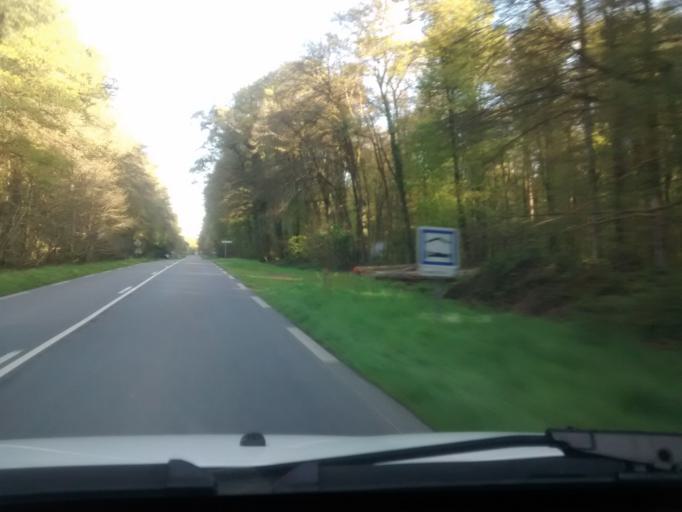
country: FR
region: Brittany
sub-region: Departement d'Ille-et-Vilaine
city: Bazouges-la-Perouse
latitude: 48.4778
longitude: -1.5501
